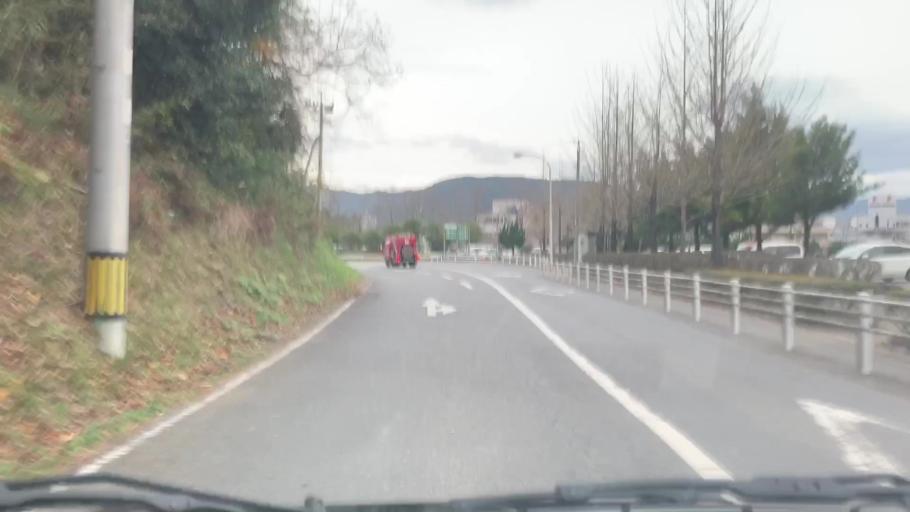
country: JP
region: Saga Prefecture
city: Takeocho-takeo
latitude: 33.1893
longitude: 130.0269
